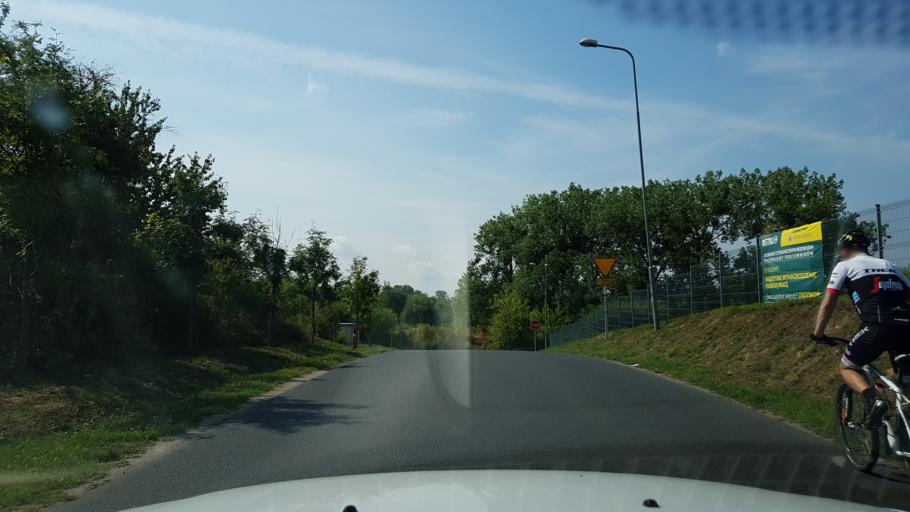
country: PL
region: West Pomeranian Voivodeship
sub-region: Powiat walecki
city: Walcz
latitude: 53.2704
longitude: 16.4914
